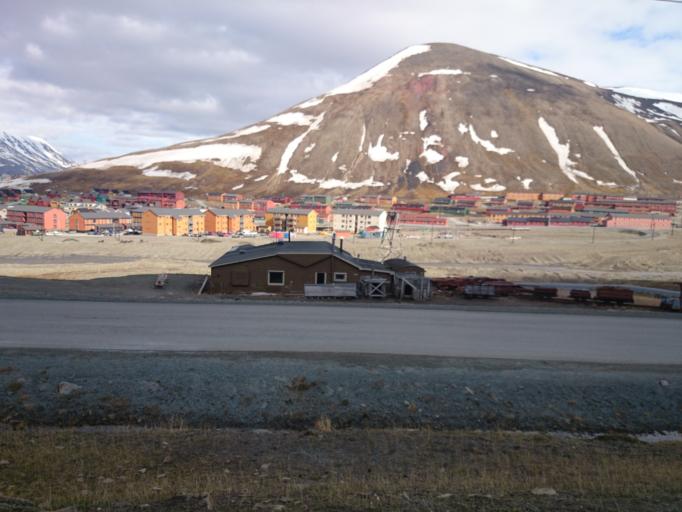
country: SJ
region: Svalbard
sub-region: Spitsbergen
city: Longyearbyen
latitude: 78.2181
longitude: 15.6167
